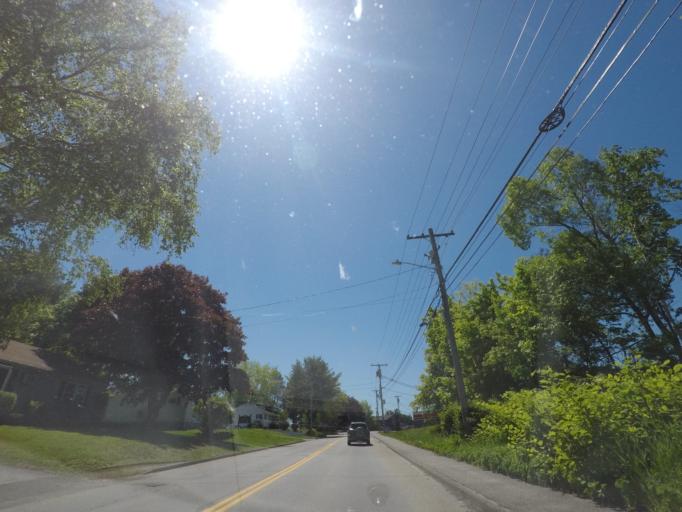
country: US
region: Maine
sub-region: Kennebec County
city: Augusta
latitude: 44.3164
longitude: -69.8024
